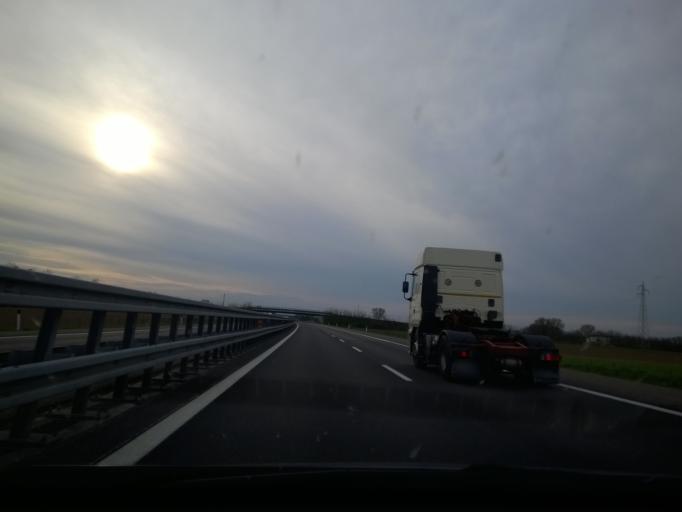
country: IT
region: Emilia-Romagna
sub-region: Provincia di Piacenza
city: Castel San Giovanni
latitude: 45.0789
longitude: 9.4305
